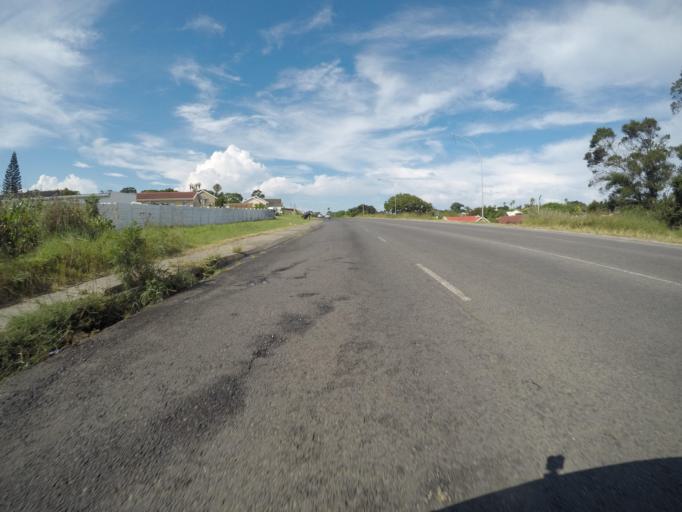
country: ZA
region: Eastern Cape
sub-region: Buffalo City Metropolitan Municipality
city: East London
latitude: -32.9925
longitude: 27.8579
